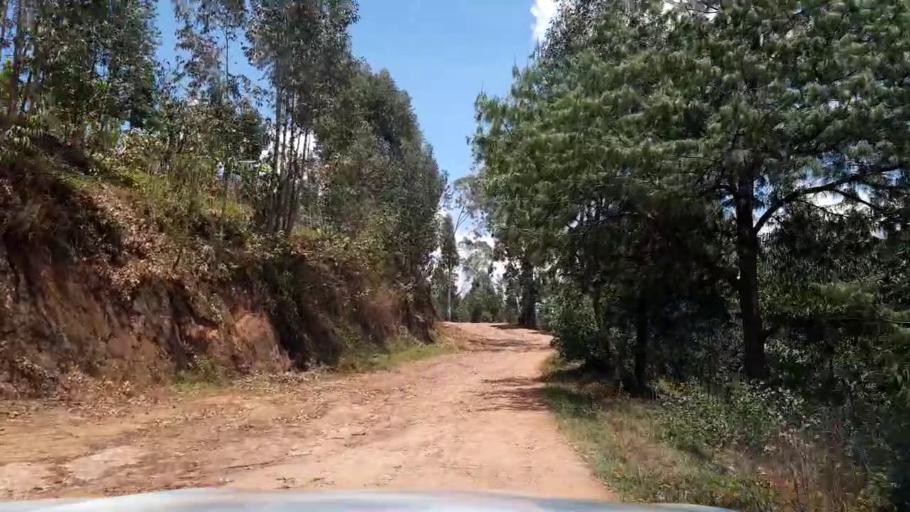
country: RW
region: Northern Province
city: Byumba
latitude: -1.5269
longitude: 30.1741
